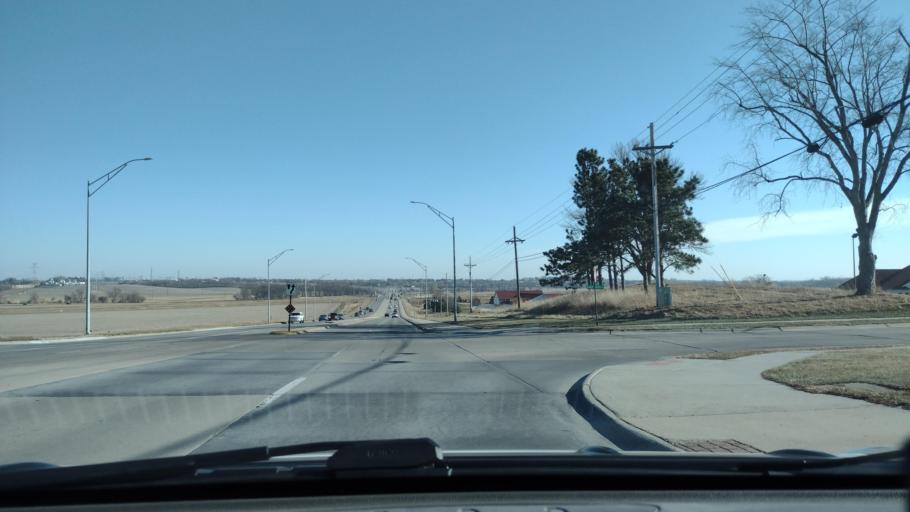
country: US
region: Nebraska
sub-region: Sarpy County
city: La Vista
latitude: 41.1617
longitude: -95.9964
